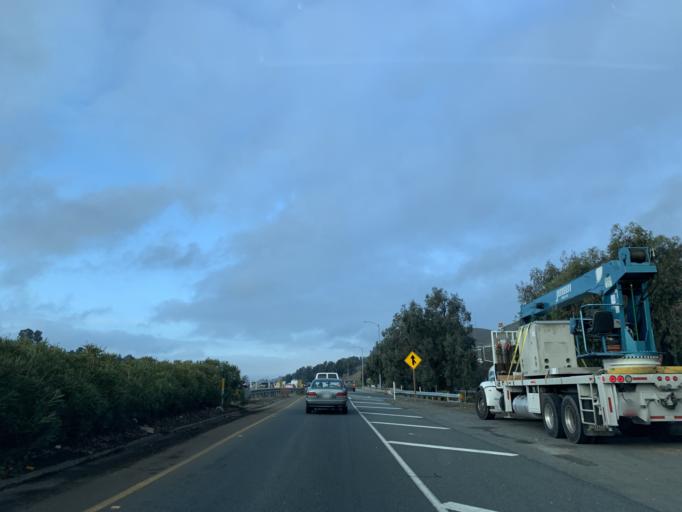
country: US
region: California
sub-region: Contra Costa County
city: Saranap
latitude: 37.8981
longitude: -122.0945
